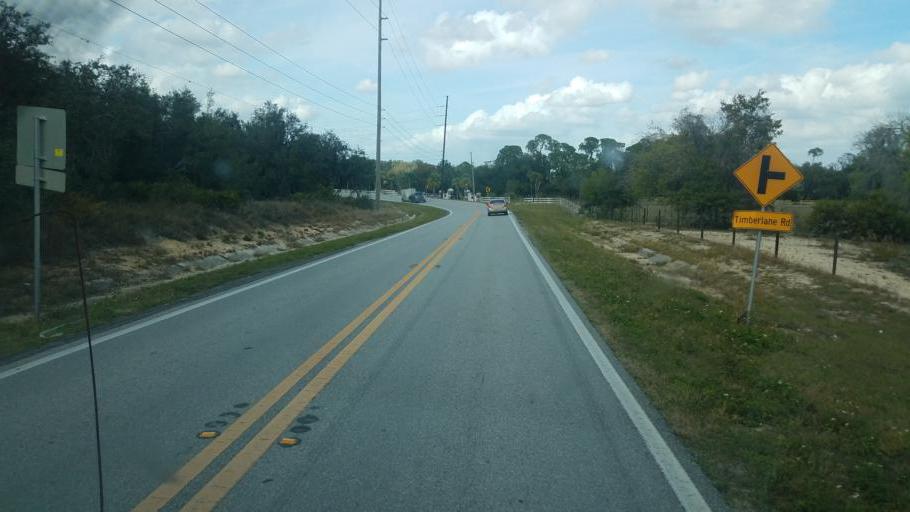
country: US
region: Florida
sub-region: Polk County
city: Lake Wales
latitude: 27.9593
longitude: -81.5379
